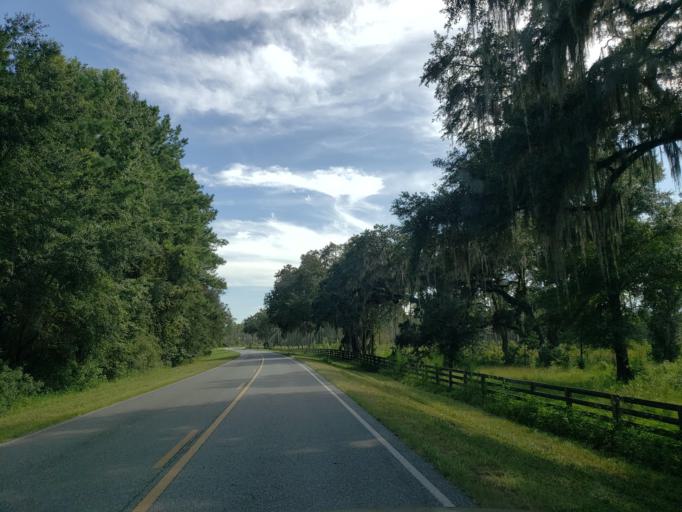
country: US
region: Georgia
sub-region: Echols County
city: Statenville
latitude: 30.6289
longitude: -83.1978
